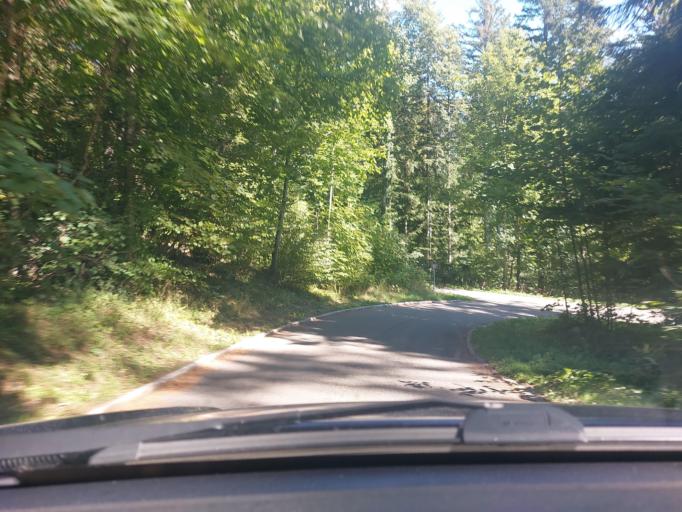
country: CH
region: Vaud
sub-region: Aigle District
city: Aigle
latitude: 46.3537
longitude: 6.9628
